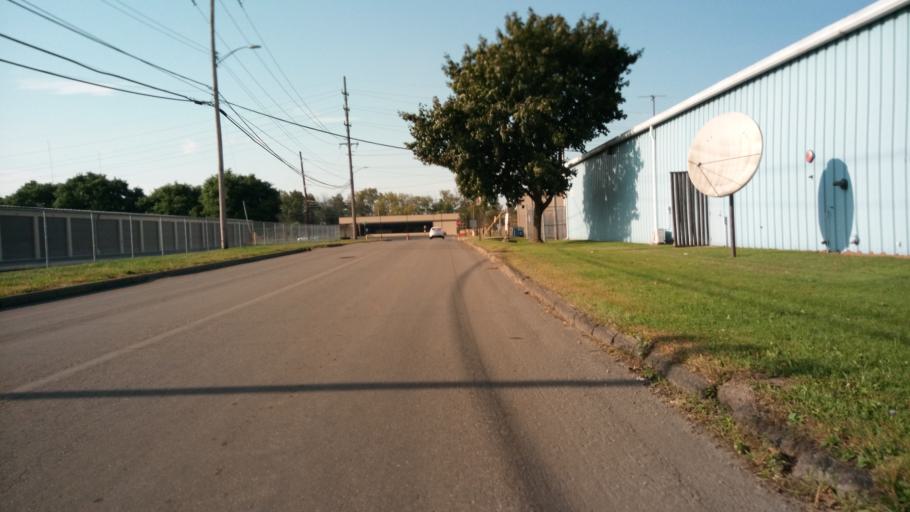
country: US
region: New York
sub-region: Chemung County
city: Elmira Heights
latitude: 42.1166
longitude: -76.8058
